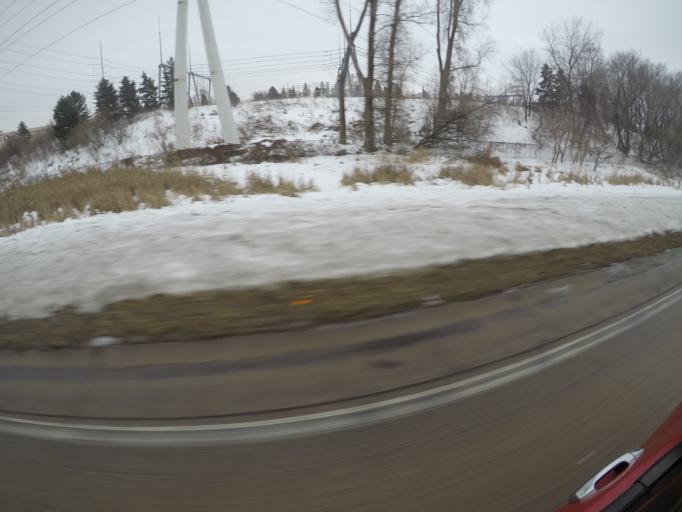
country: US
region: Minnesota
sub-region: Hennepin County
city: Eden Prairie
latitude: 44.8637
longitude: -93.4347
